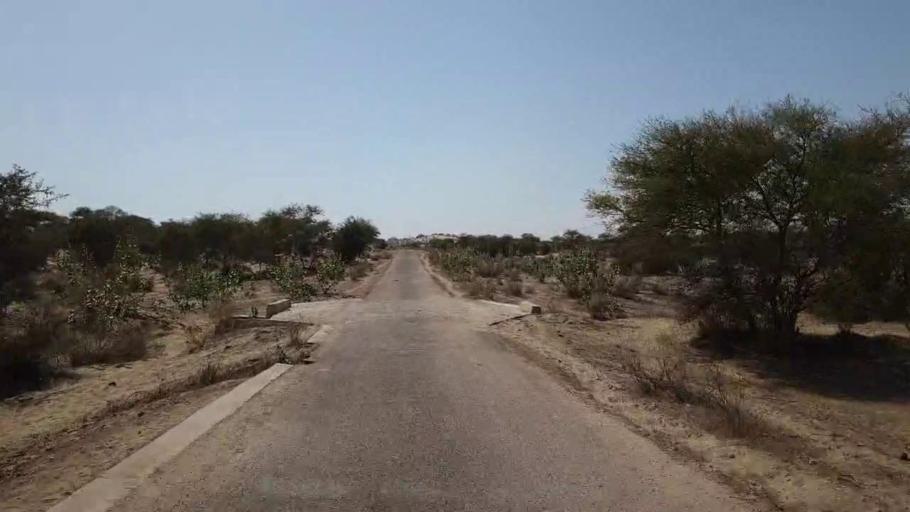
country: PK
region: Sindh
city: Umarkot
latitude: 25.2219
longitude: 69.8827
